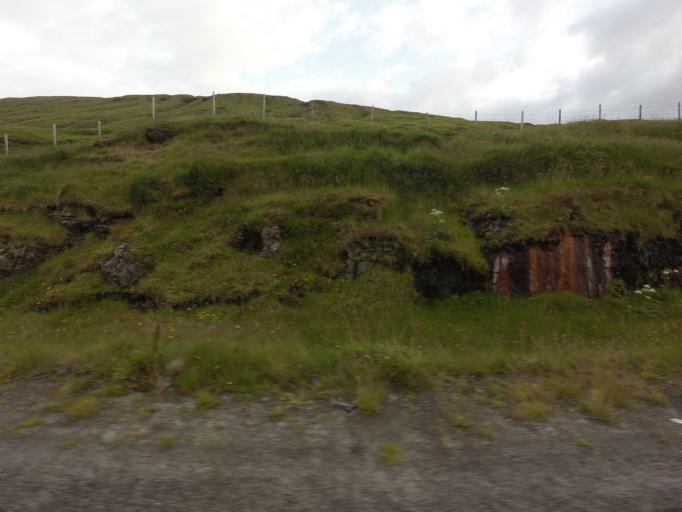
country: FO
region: Streymoy
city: Kollafjordhur
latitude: 62.1703
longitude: -6.9670
